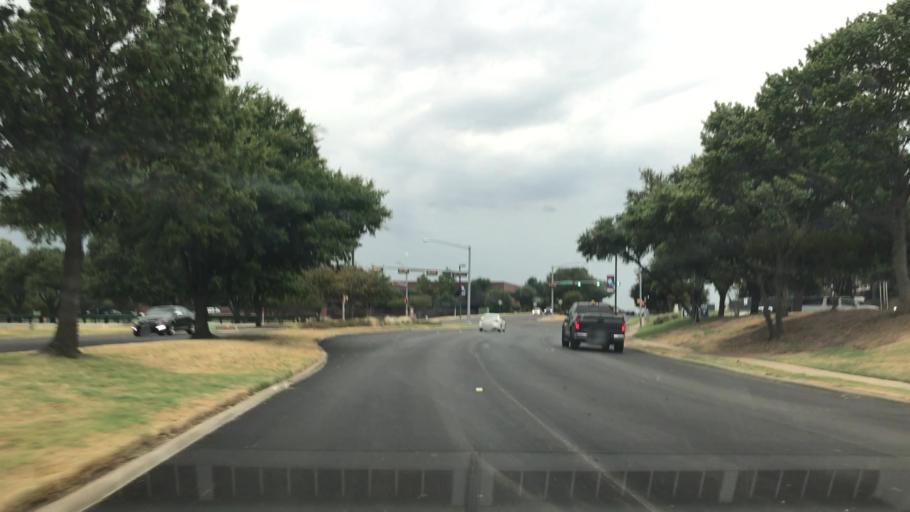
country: US
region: Texas
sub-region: Dallas County
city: Farmers Branch
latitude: 32.9446
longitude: -96.9522
